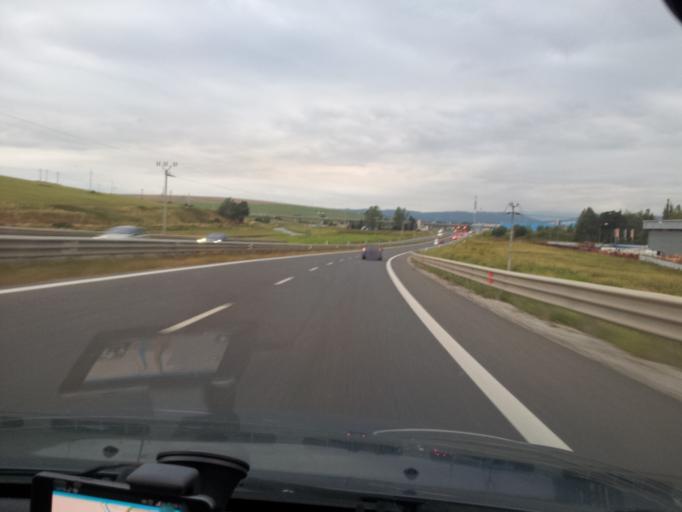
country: SK
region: Presovsky
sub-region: Okres Poprad
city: Poprad
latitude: 49.0802
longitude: 20.3321
